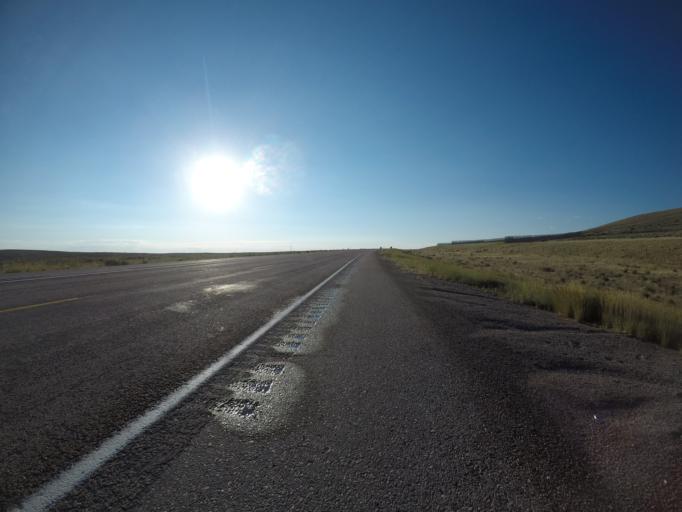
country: US
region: Wyoming
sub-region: Lincoln County
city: Kemmerer
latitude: 41.8912
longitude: -110.4024
